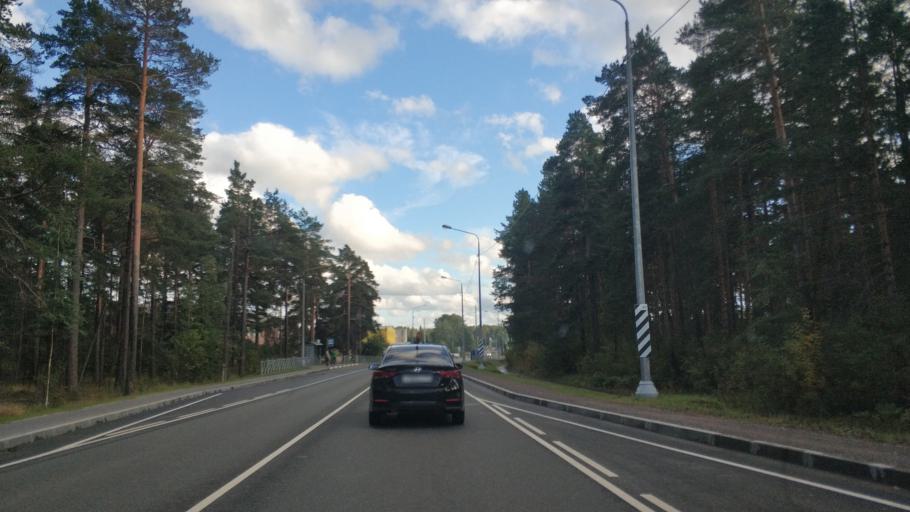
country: RU
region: Leningrad
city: Priozersk
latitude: 61.0040
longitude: 30.1803
